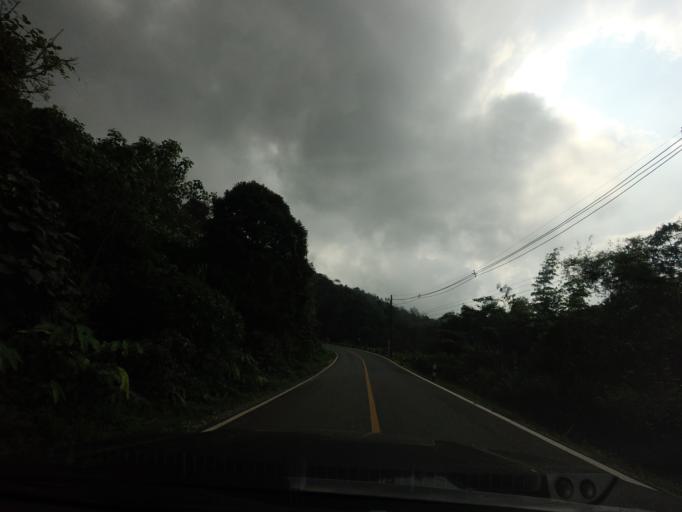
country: TH
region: Nan
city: Bo Kluea
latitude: 19.1876
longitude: 101.0781
